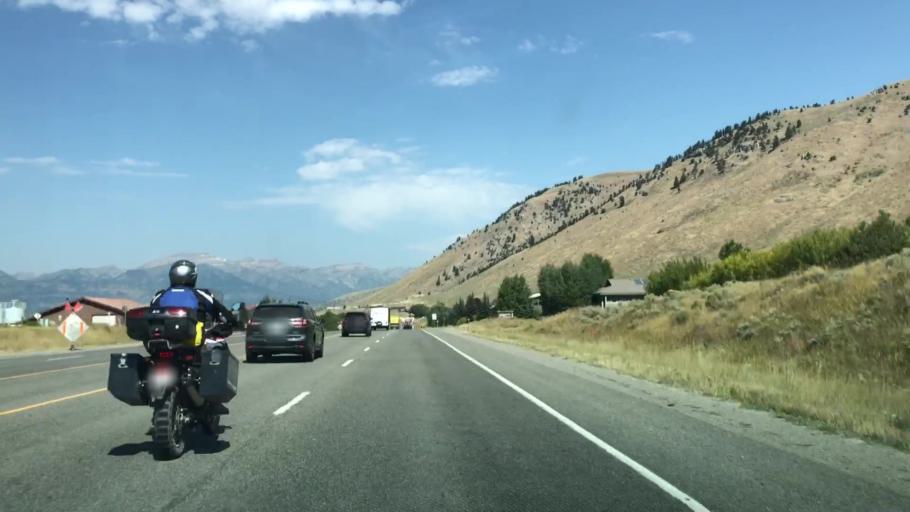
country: US
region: Wyoming
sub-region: Teton County
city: South Park
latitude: 43.4198
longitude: -110.7753
